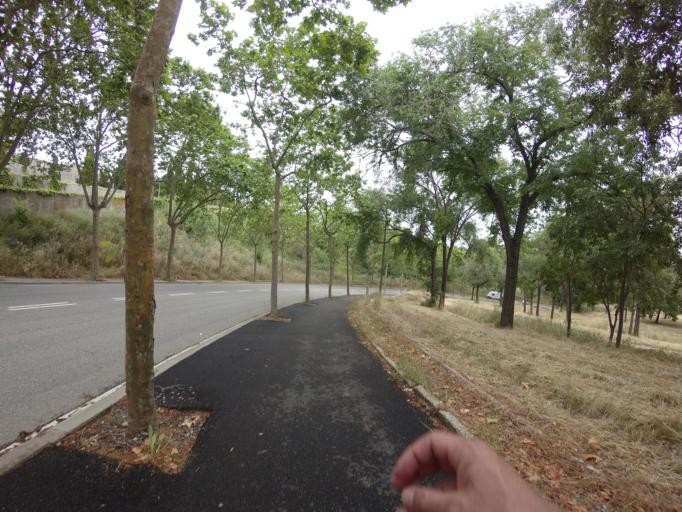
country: ES
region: Catalonia
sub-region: Provincia de Barcelona
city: Sants-Montjuic
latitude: 41.3592
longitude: 2.1546
